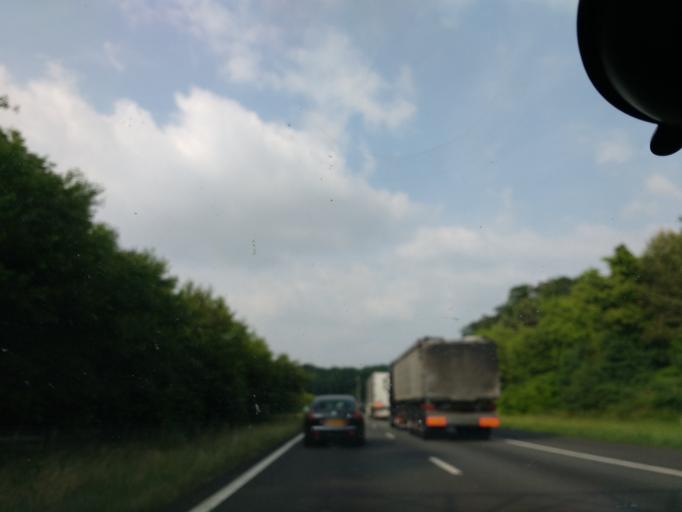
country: NL
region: Gelderland
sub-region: Gemeente Renkum
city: Wolfheze
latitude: 52.0244
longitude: 5.8225
